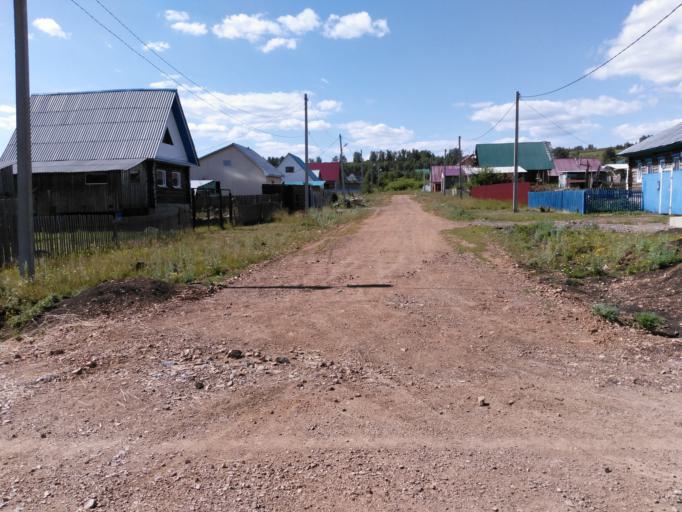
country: RU
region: Bashkortostan
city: Uchaly
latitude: 54.2883
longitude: 59.3603
